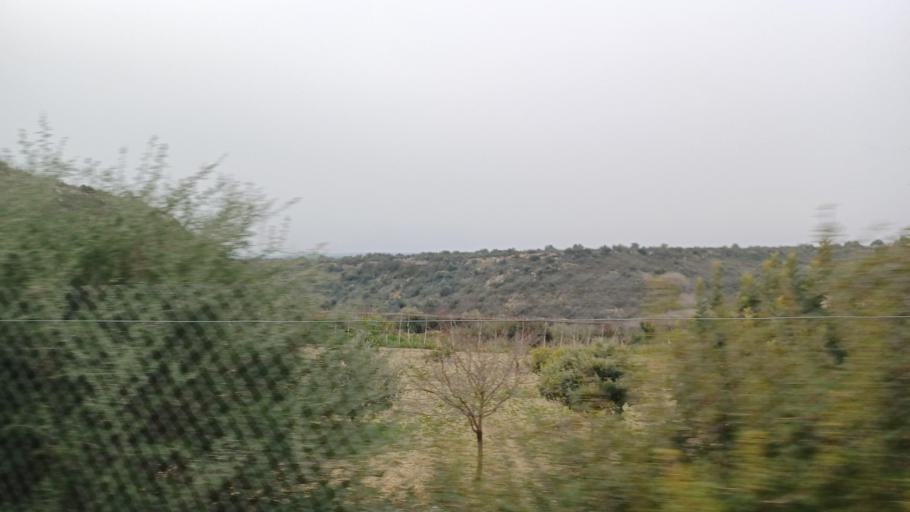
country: CY
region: Limassol
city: Pissouri
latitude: 34.7204
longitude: 32.7379
